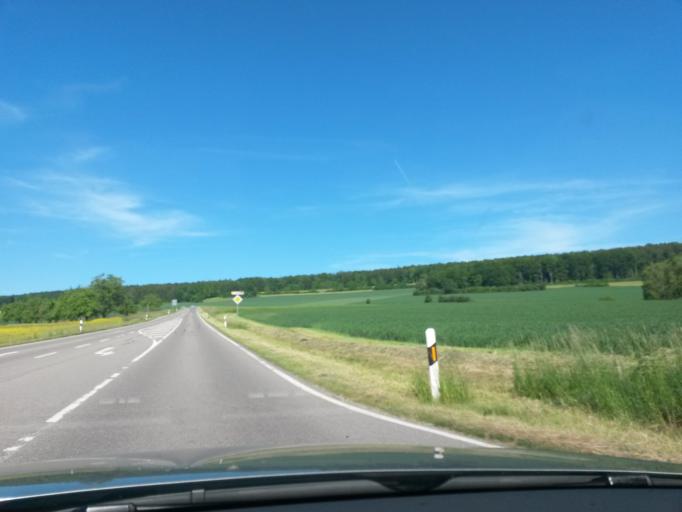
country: DE
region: Baden-Wuerttemberg
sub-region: Tuebingen Region
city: Langenenslingen
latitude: 48.1743
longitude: 9.4111
